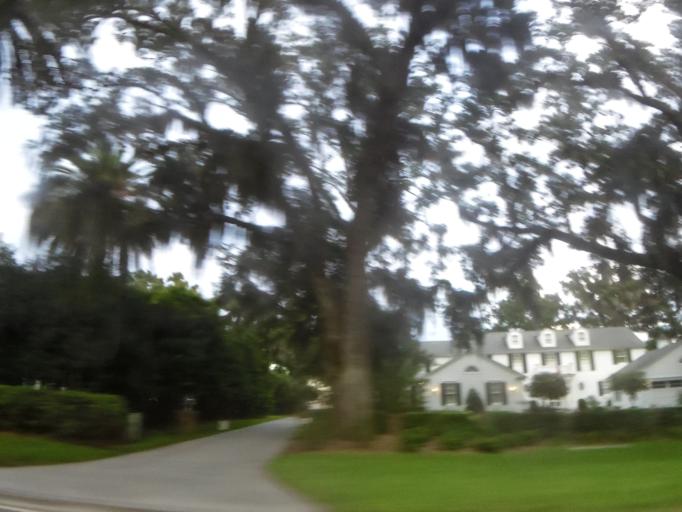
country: US
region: Florida
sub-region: Duval County
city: Jacksonville
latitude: 30.2653
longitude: -81.6992
